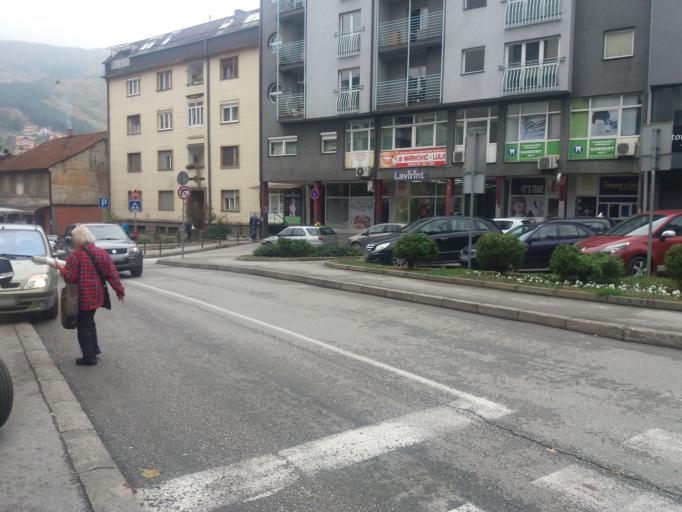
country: RS
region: Central Serbia
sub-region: Zlatiborski Okrug
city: Uzice
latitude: 43.8574
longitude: 19.8392
